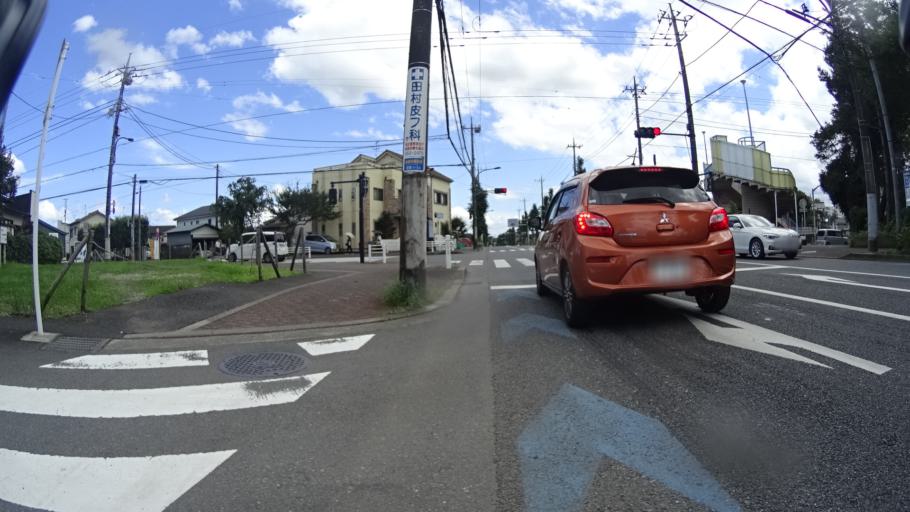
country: JP
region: Tokyo
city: Fussa
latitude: 35.7570
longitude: 139.3139
